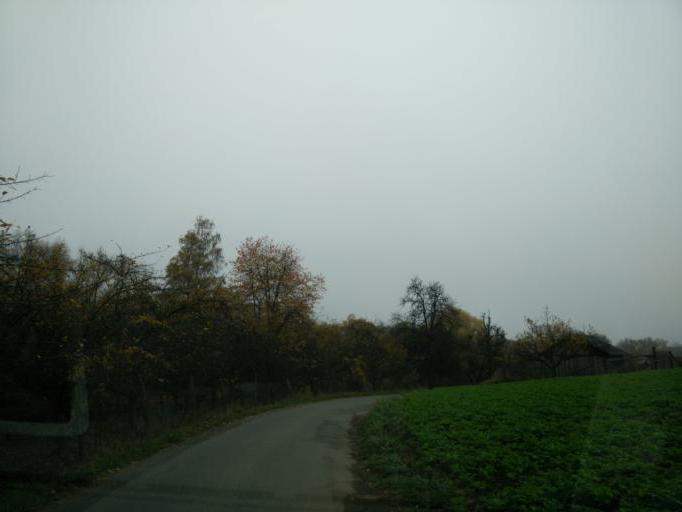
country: DE
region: Baden-Wuerttemberg
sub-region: Tuebingen Region
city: Rottenburg
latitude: 48.5348
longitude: 8.9786
